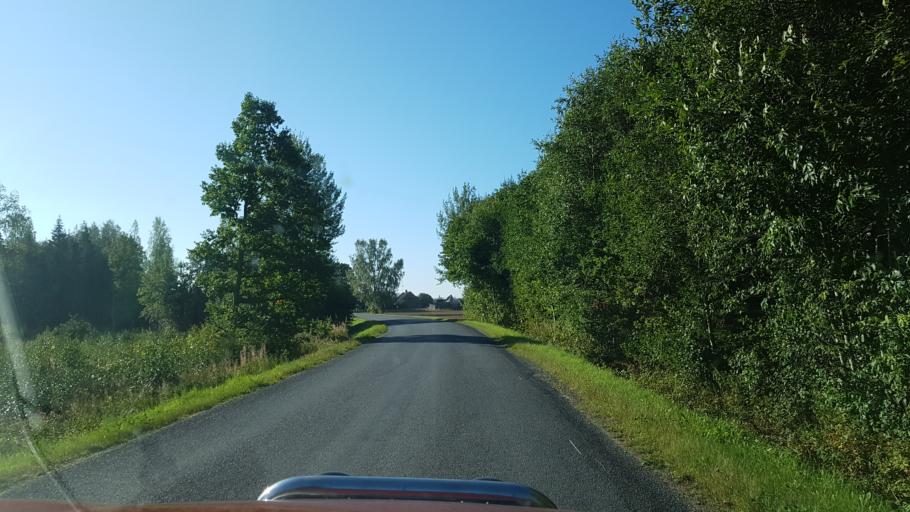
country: EE
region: Jogevamaa
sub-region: Jogeva linn
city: Jogeva
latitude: 58.7196
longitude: 26.5175
